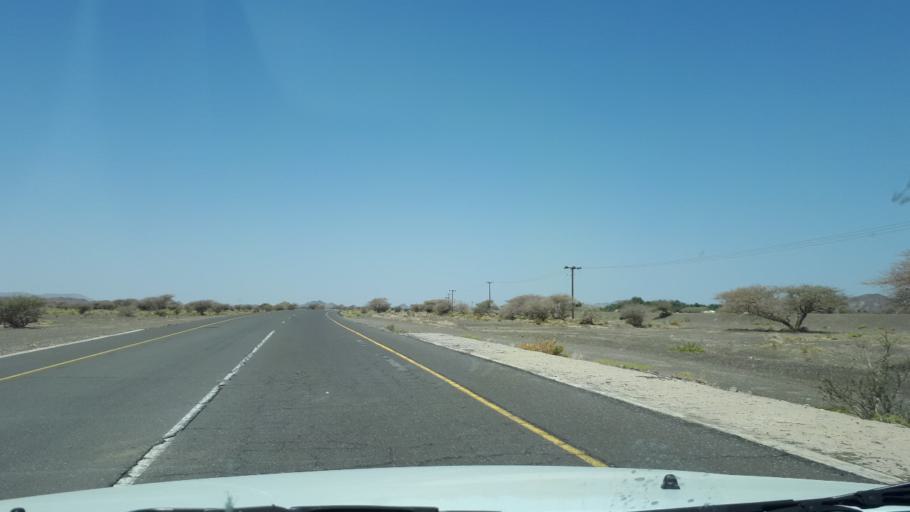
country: OM
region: Ash Sharqiyah
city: Ibra'
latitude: 22.6170
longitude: 58.4271
